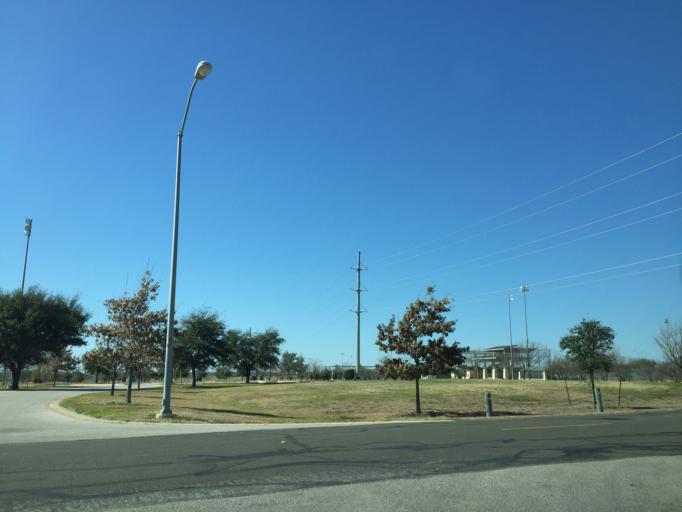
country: US
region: Texas
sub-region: Williamson County
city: Hutto
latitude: 30.5450
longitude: -97.6176
